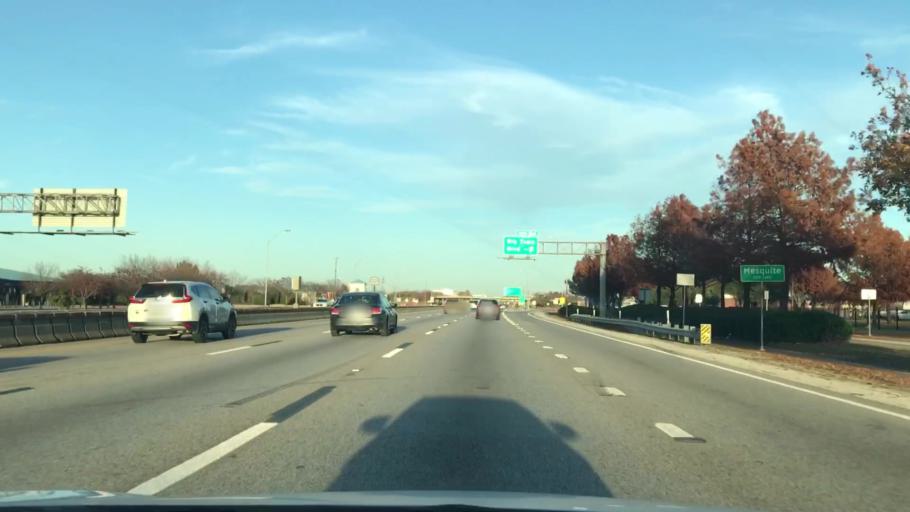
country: US
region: Texas
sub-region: Dallas County
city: Mesquite
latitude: 32.8009
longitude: -96.6742
